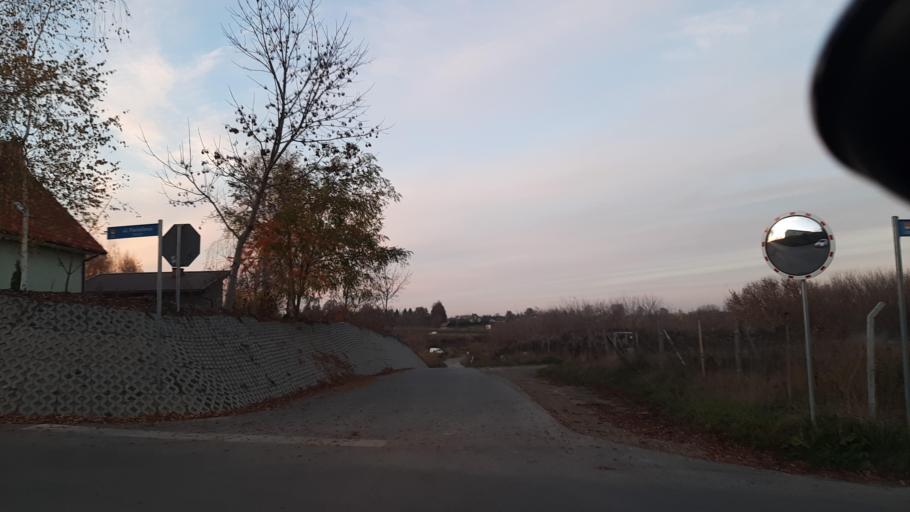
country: PL
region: Lublin Voivodeship
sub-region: Powiat lubelski
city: Jastkow
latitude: 51.2990
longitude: 22.5036
